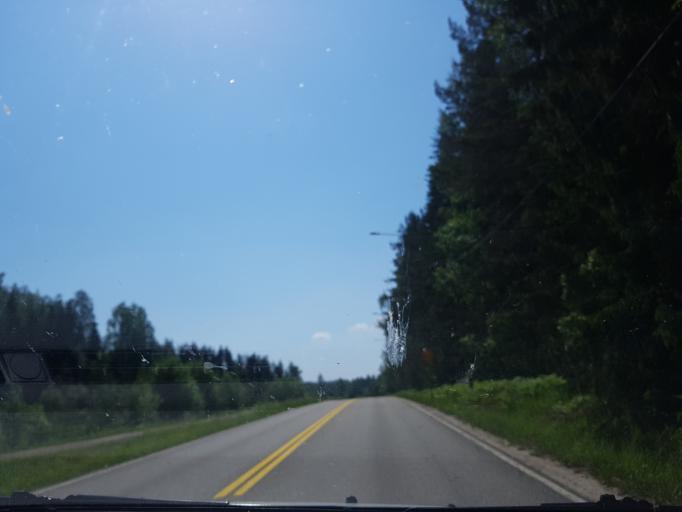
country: FI
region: Uusimaa
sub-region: Helsinki
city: Vihti
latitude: 60.3255
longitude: 24.4079
